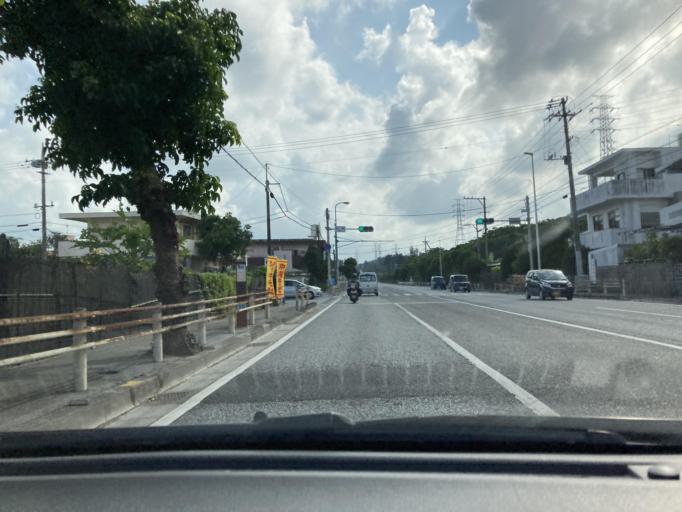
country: JP
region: Okinawa
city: Ginowan
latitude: 26.2605
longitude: 127.7873
